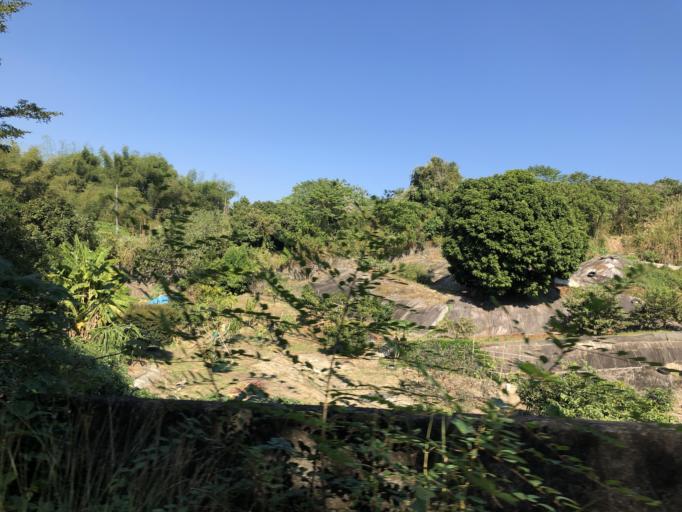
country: TW
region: Taiwan
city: Yujing
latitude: 23.0526
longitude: 120.3804
